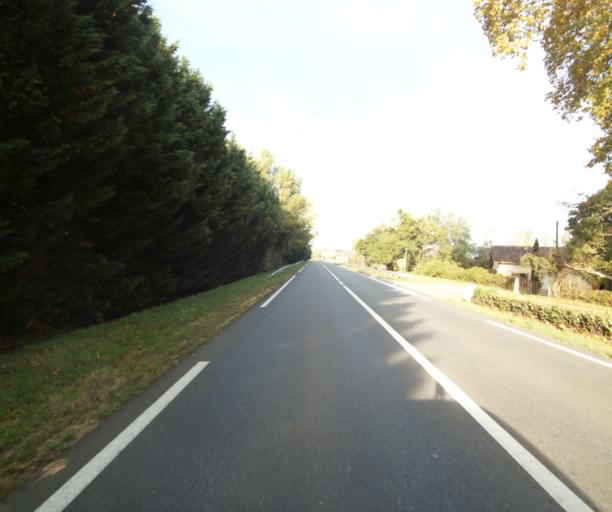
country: FR
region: Midi-Pyrenees
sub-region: Departement de la Haute-Garonne
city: Villemur-sur-Tarn
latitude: 43.9282
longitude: 1.5048
